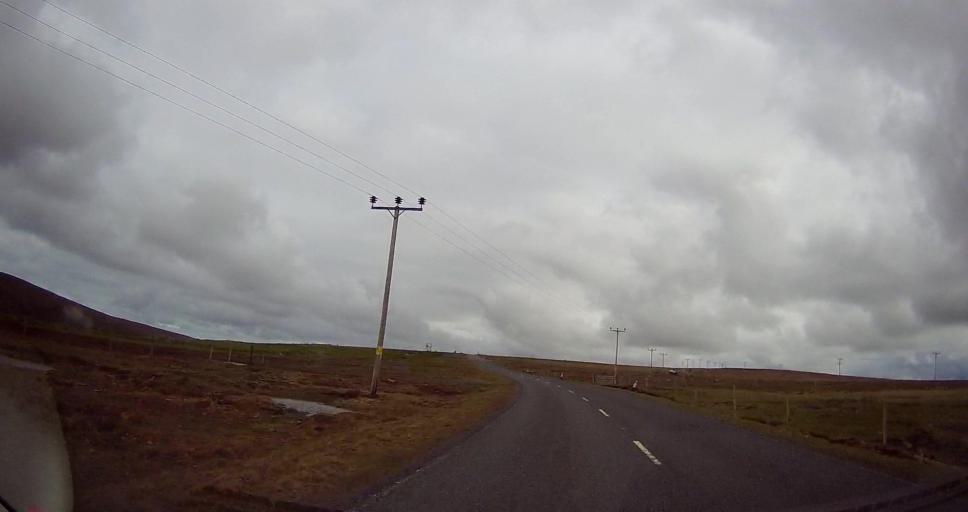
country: GB
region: Scotland
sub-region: Shetland Islands
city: Shetland
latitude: 60.7314
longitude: -0.8959
